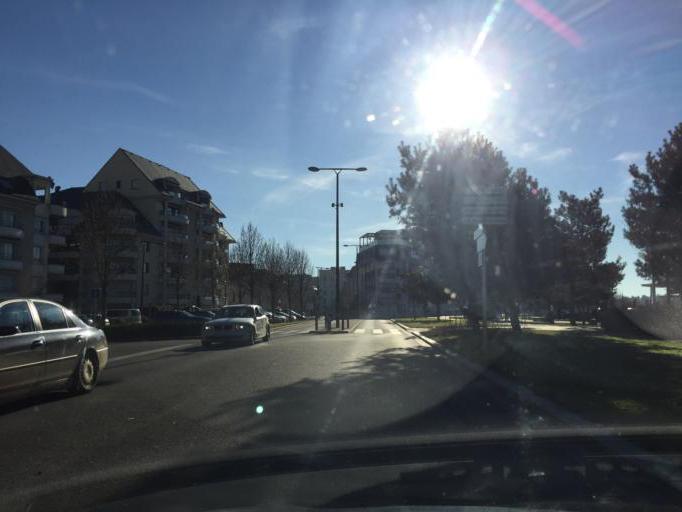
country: FR
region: Auvergne
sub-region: Departement de l'Allier
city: Vichy
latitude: 46.1298
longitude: 3.4159
